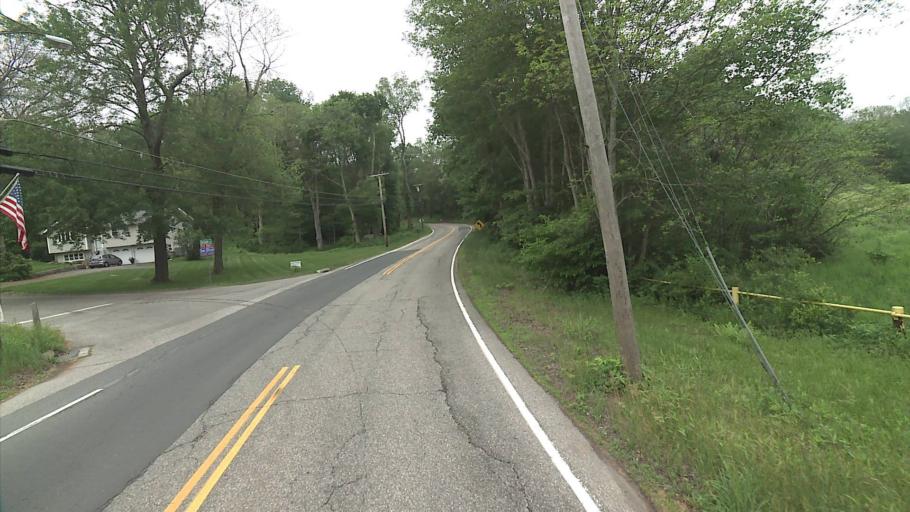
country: US
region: Connecticut
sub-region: Tolland County
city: Coventry Lake
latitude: 41.7289
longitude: -72.3703
